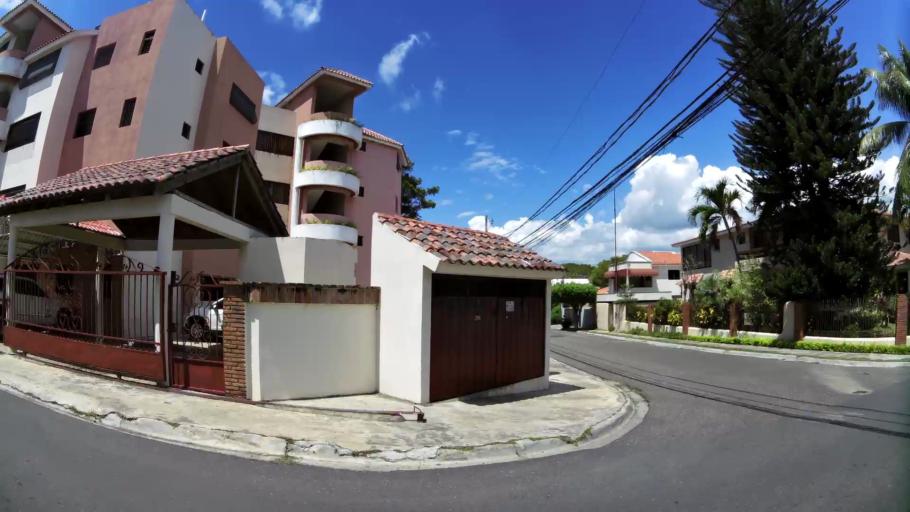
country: DO
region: Santiago
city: Santiago de los Caballeros
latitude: 19.4709
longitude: -70.6780
